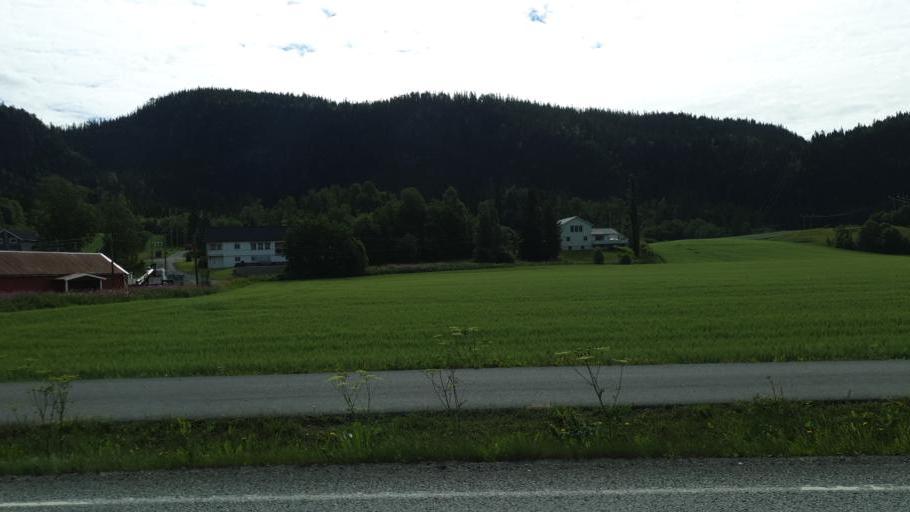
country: NO
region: Sor-Trondelag
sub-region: Melhus
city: Lundamo
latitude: 63.1628
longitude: 10.3035
